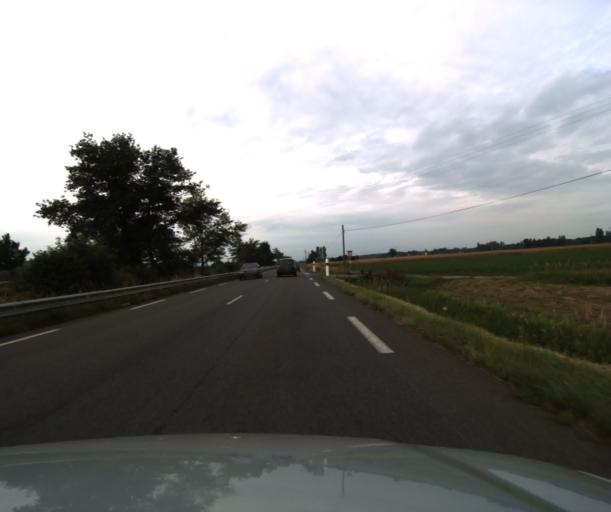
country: FR
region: Midi-Pyrenees
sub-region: Departement des Hautes-Pyrenees
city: Rabastens-de-Bigorre
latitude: 43.3602
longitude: 0.1404
